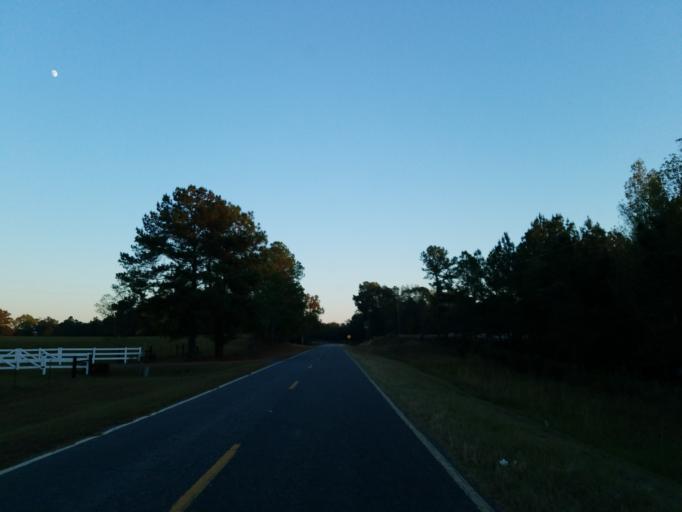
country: US
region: Georgia
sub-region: Ben Hill County
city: Fitzgerald
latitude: 31.6542
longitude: -83.3884
